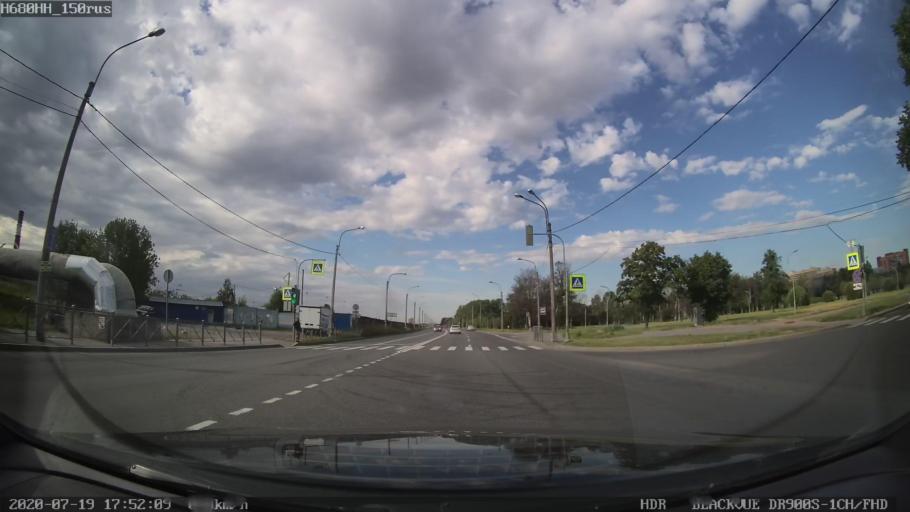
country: RU
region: St.-Petersburg
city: Avtovo
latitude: 59.8644
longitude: 30.2953
